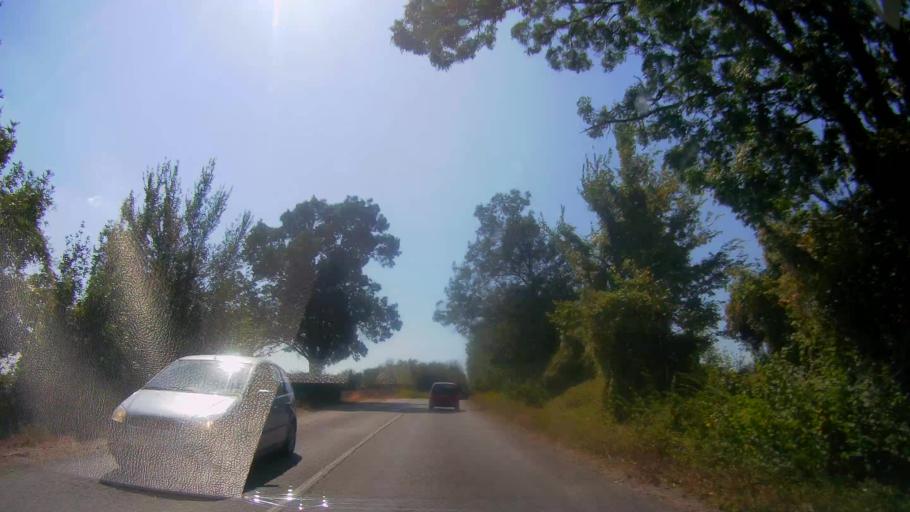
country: BG
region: Veliko Turnovo
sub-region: Obshtina Gorna Oryakhovitsa
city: Purvomaytsi
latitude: 43.2473
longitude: 25.6445
